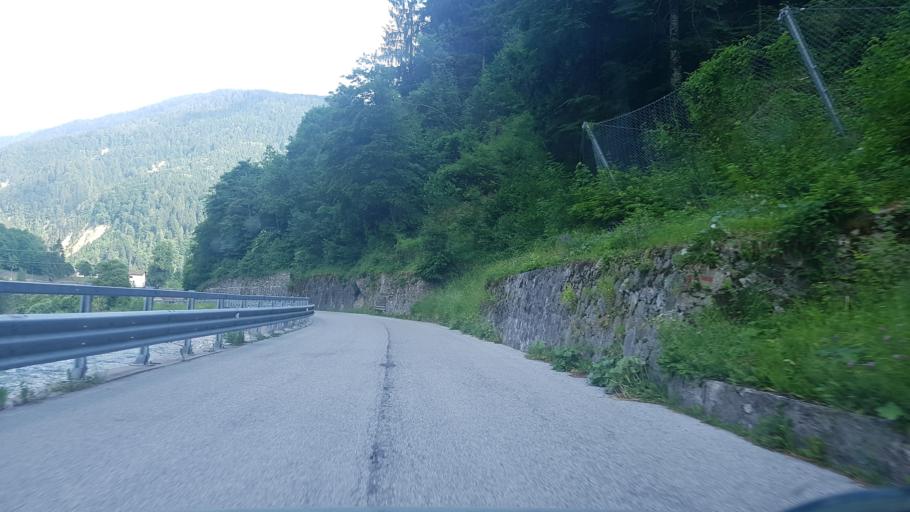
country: IT
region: Friuli Venezia Giulia
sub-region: Provincia di Udine
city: Pontebba
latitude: 46.5115
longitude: 13.2972
